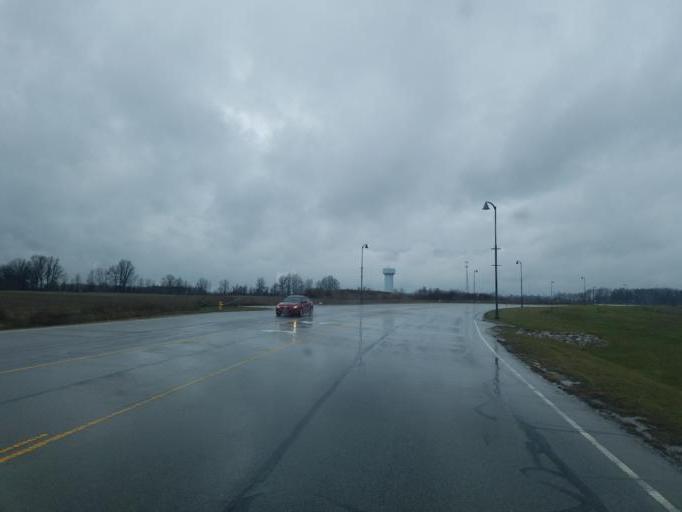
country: US
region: Ohio
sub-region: Delaware County
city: Sunbury
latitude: 40.2739
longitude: -82.9158
